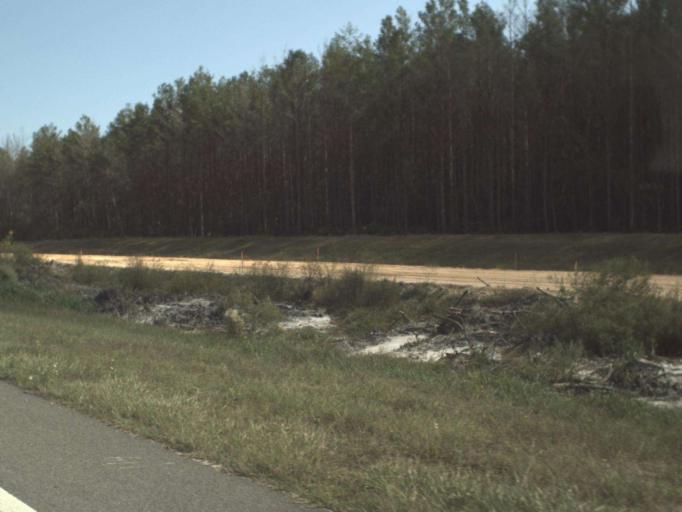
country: US
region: Florida
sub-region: Walton County
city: Freeport
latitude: 30.5063
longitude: -86.1150
